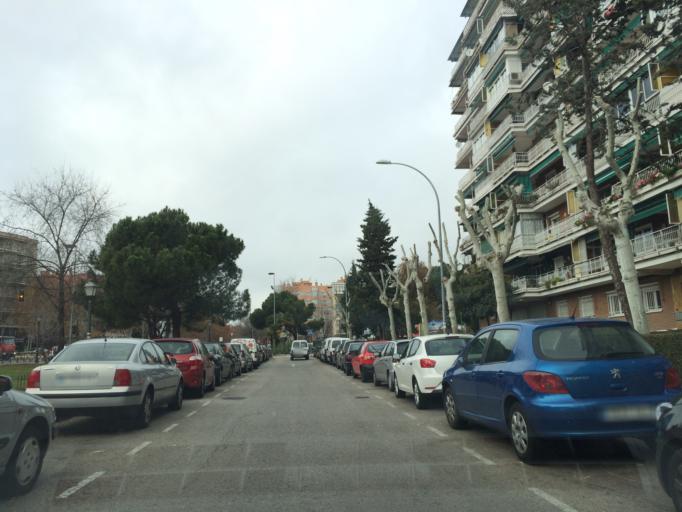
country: ES
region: Madrid
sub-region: Provincia de Madrid
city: Alcorcon
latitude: 40.3506
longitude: -3.8225
